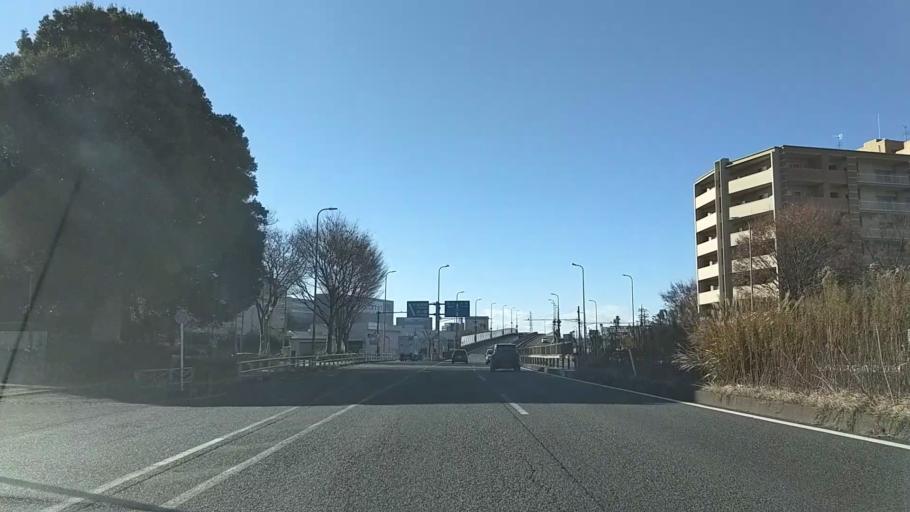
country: JP
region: Kanagawa
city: Minami-rinkan
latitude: 35.5029
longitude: 139.4700
